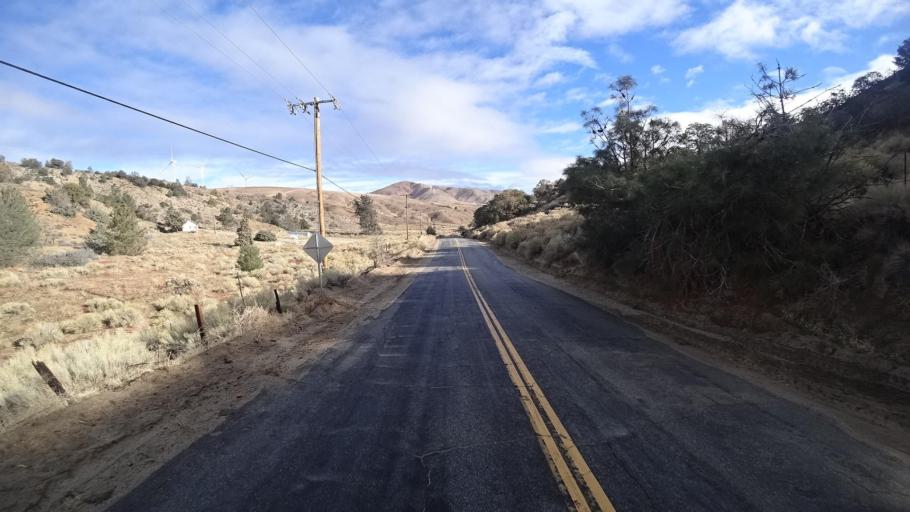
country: US
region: California
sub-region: Kern County
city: Tehachapi
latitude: 35.0831
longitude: -118.3260
